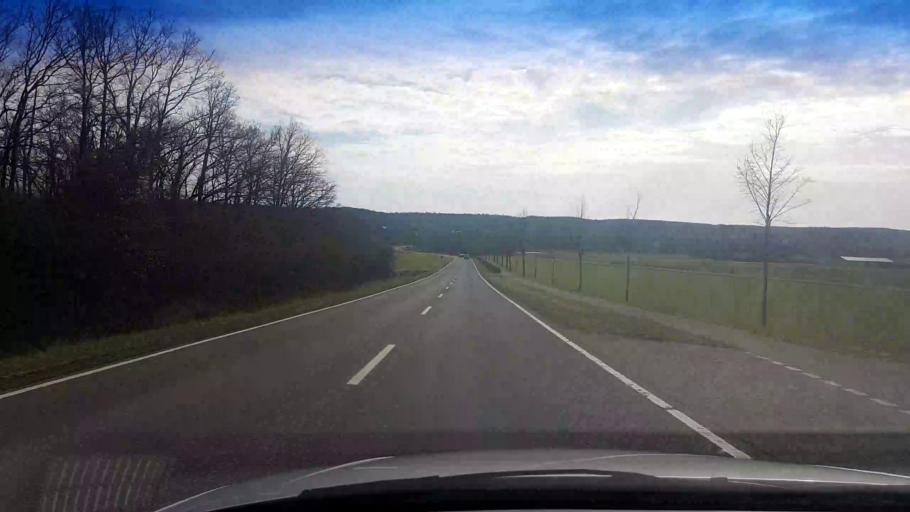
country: DE
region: Bavaria
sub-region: Upper Franconia
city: Frensdorf
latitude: 49.8266
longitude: 10.8667
